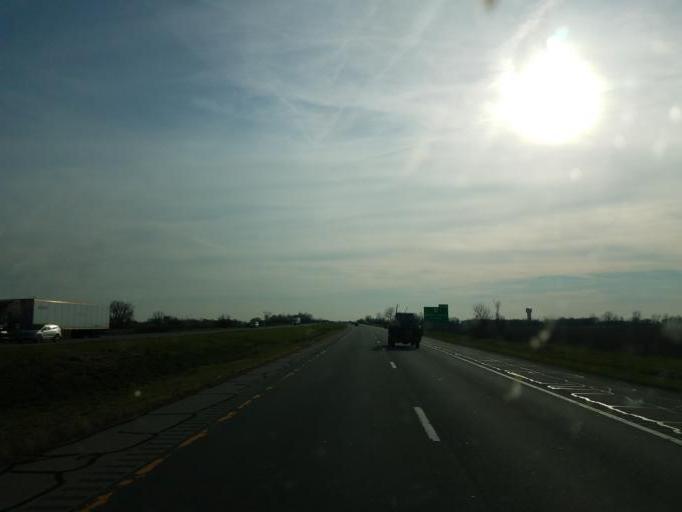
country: US
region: Ohio
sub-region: Madison County
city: Bethel
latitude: 39.7027
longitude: -83.4429
